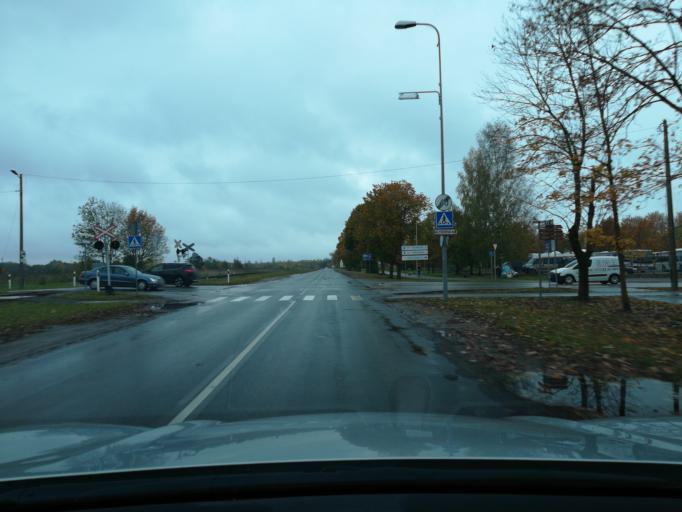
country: EE
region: Ida-Virumaa
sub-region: Johvi vald
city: Johvi
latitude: 59.3222
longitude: 27.4246
